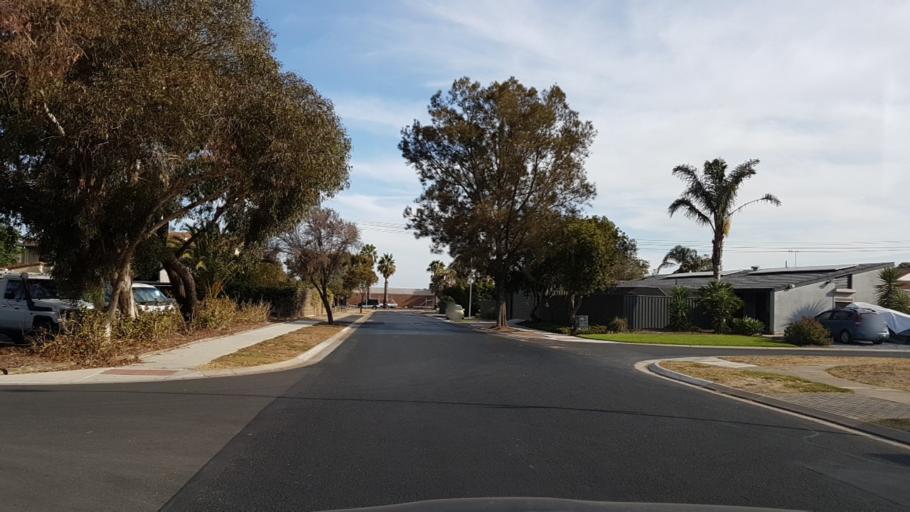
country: AU
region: South Australia
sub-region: Charles Sturt
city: West Lakes Shore
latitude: -34.8565
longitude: 138.4967
